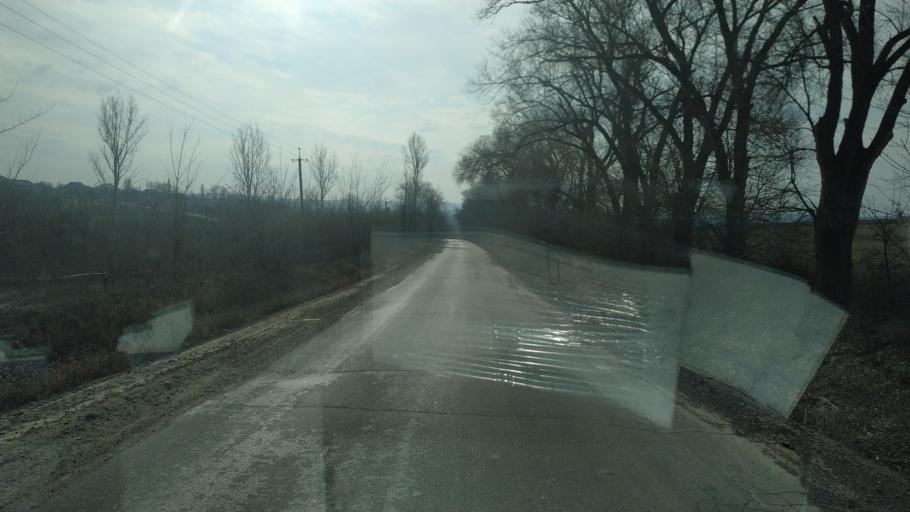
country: MD
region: Chisinau
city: Singera
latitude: 46.9314
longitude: 29.0476
